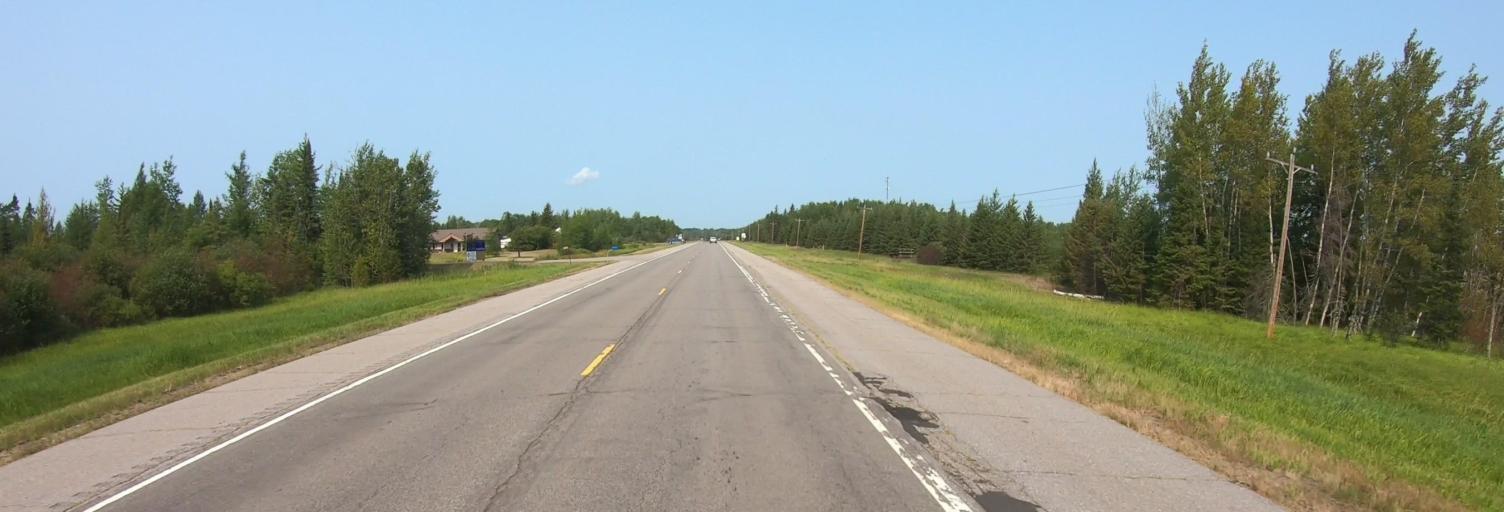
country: US
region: Minnesota
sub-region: Saint Louis County
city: Mountain Iron
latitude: 47.8557
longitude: -92.7025
